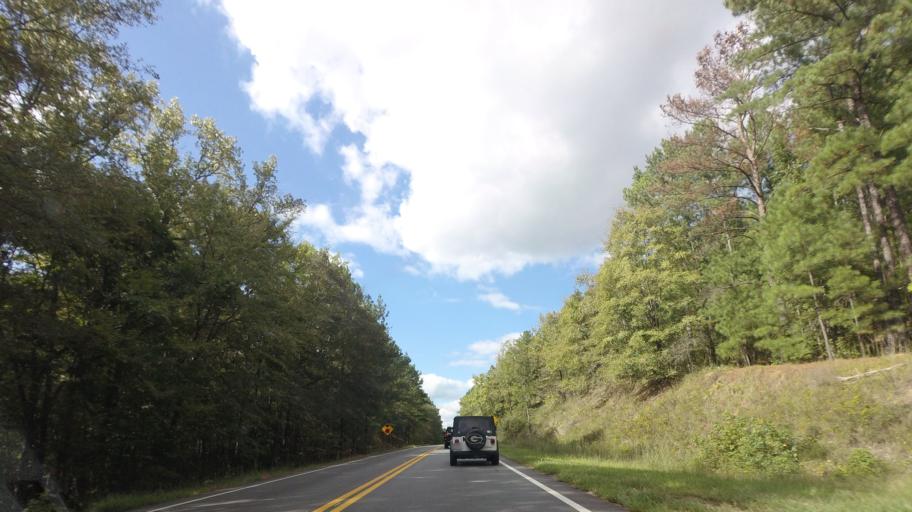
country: US
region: Georgia
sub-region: Monroe County
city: Forsyth
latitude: 33.0199
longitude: -83.7441
